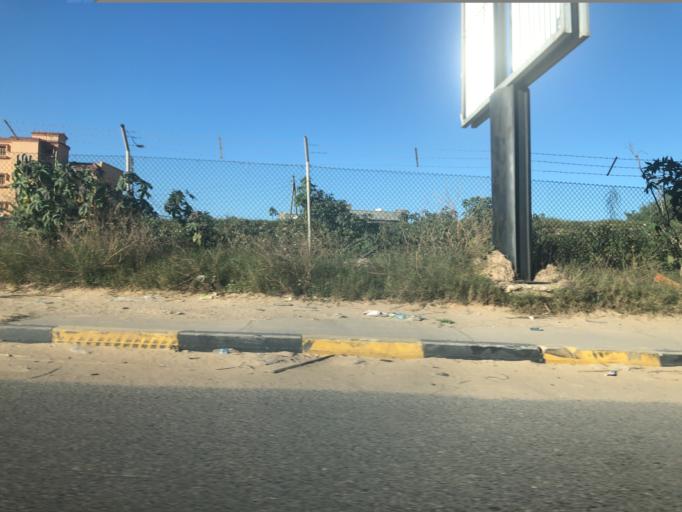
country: LY
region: Tripoli
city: Tripoli
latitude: 32.8701
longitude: 13.2652
